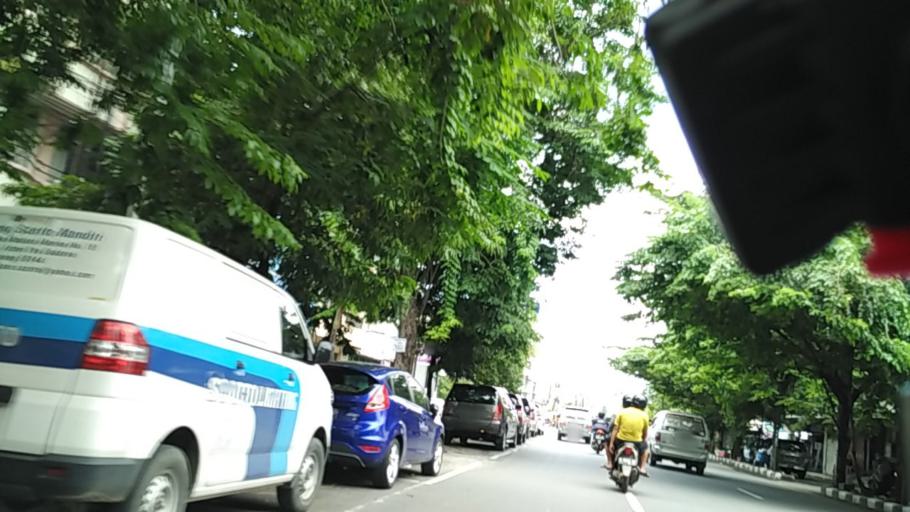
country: ID
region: Central Java
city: Semarang
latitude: -6.9866
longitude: 110.4316
